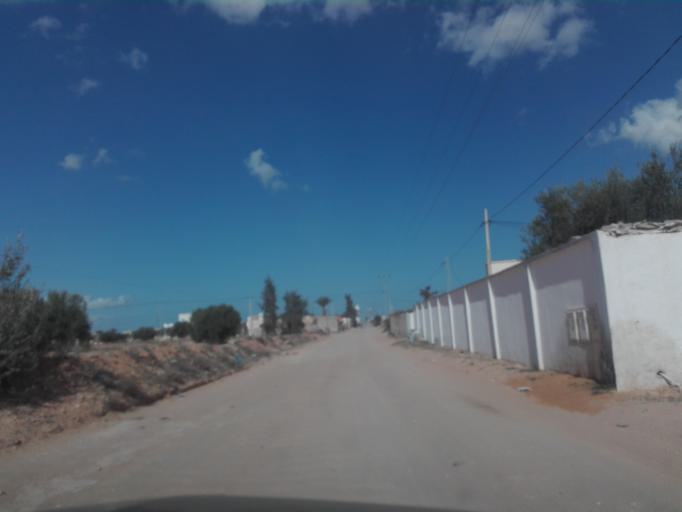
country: TN
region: Madanin
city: Bin Qirdan
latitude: 33.1544
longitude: 11.1935
